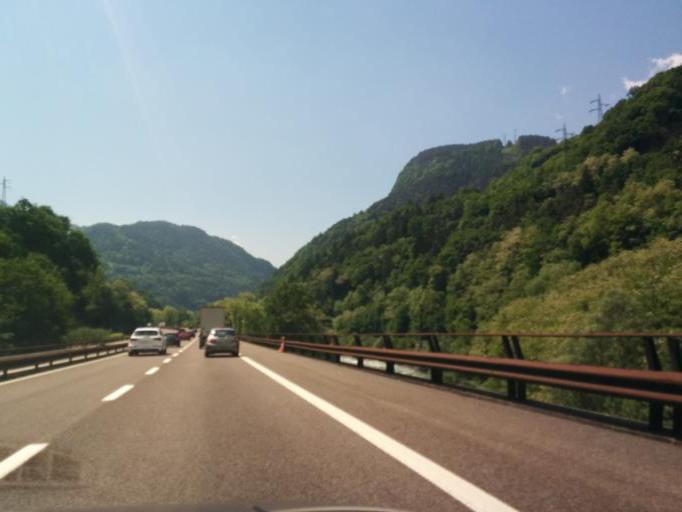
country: IT
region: Trentino-Alto Adige
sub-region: Bolzano
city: Ponte Gardena
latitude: 46.5797
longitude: 11.5236
